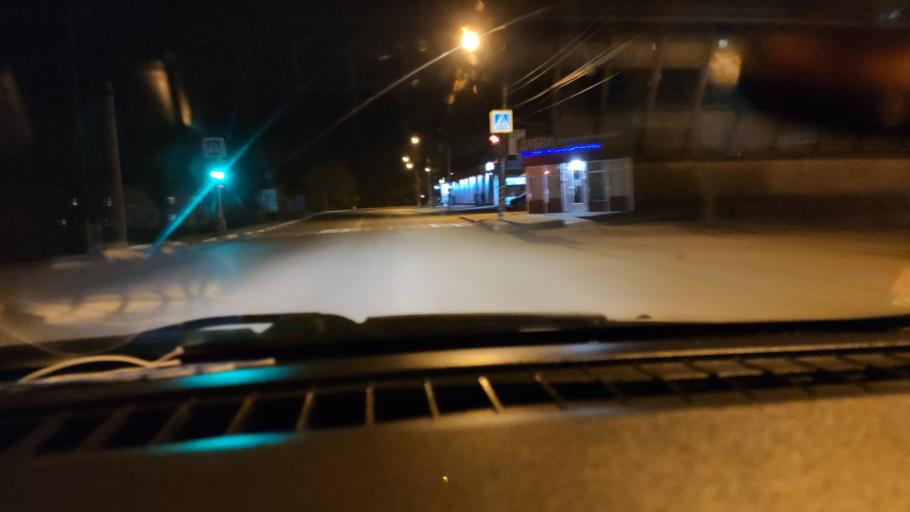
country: RU
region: Saratov
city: Privolzhskiy
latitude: 51.3914
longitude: 46.0351
